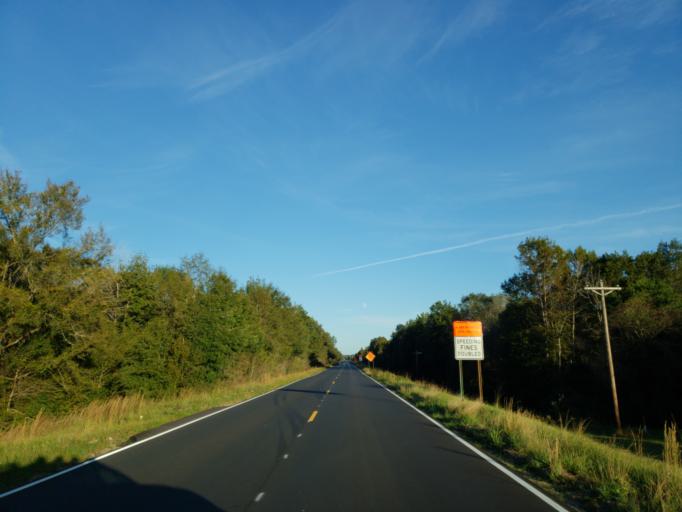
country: US
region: Mississippi
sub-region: Wayne County
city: Belmont
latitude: 31.4239
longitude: -88.5496
